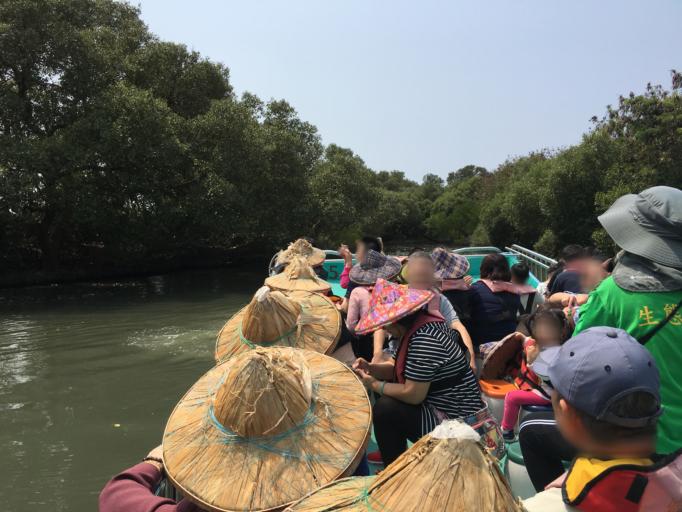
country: TW
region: Taiwan
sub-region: Tainan
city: Tainan
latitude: 23.0257
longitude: 120.1355
